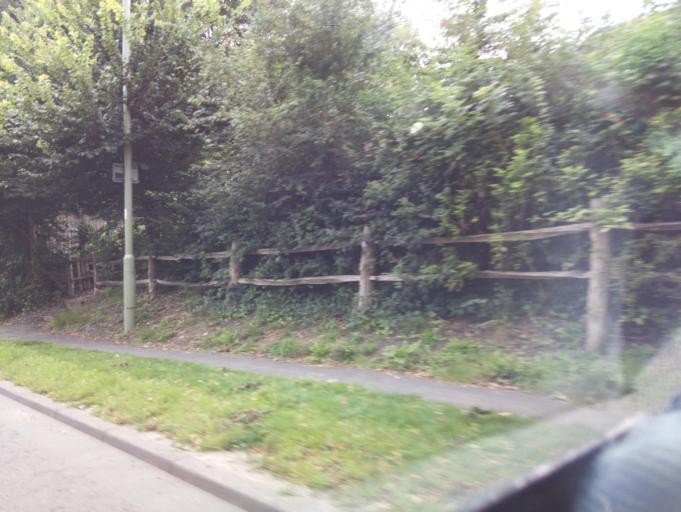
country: GB
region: England
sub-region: Hampshire
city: Lymington
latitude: 50.7524
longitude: -1.5523
